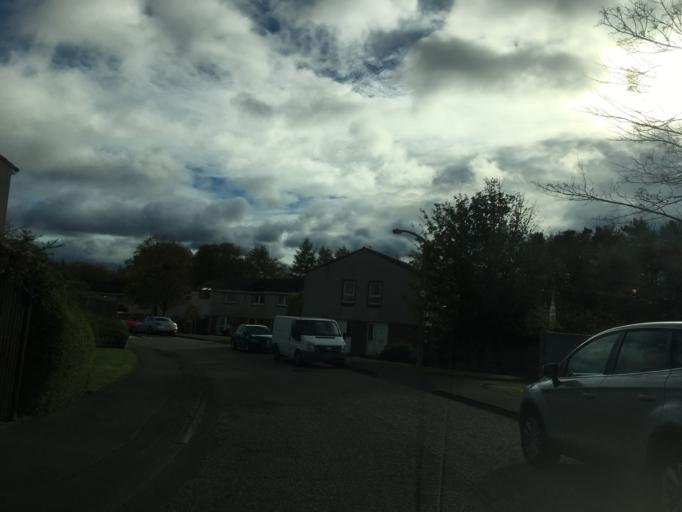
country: GB
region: Scotland
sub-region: Midlothian
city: Loanhead
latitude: 55.9041
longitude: -3.1748
